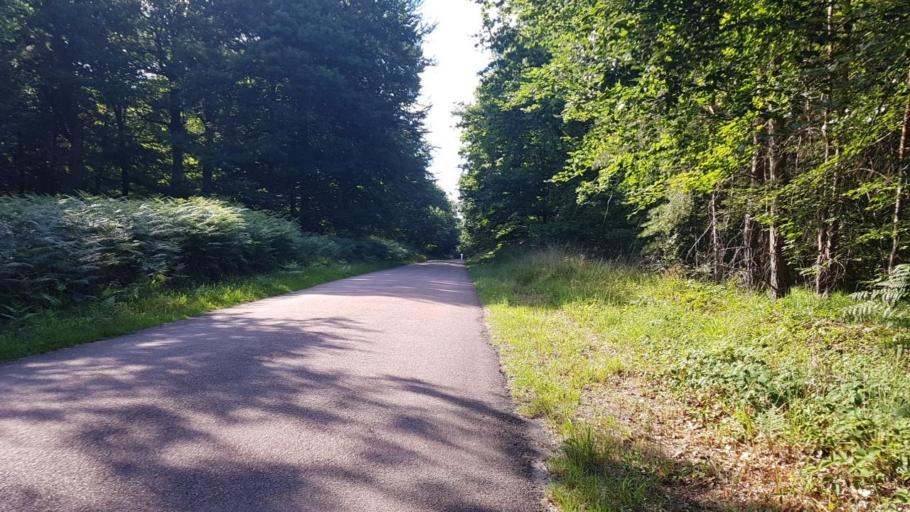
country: FR
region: Picardie
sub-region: Departement de l'Oise
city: Ver-sur-Launette
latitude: 49.1492
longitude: 2.6431
